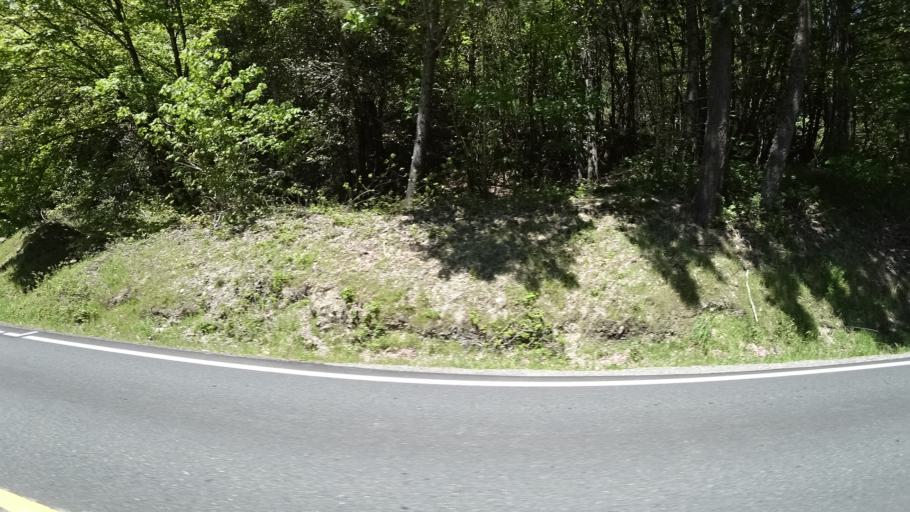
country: US
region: California
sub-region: Humboldt County
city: Willow Creek
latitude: 40.9307
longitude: -123.6867
